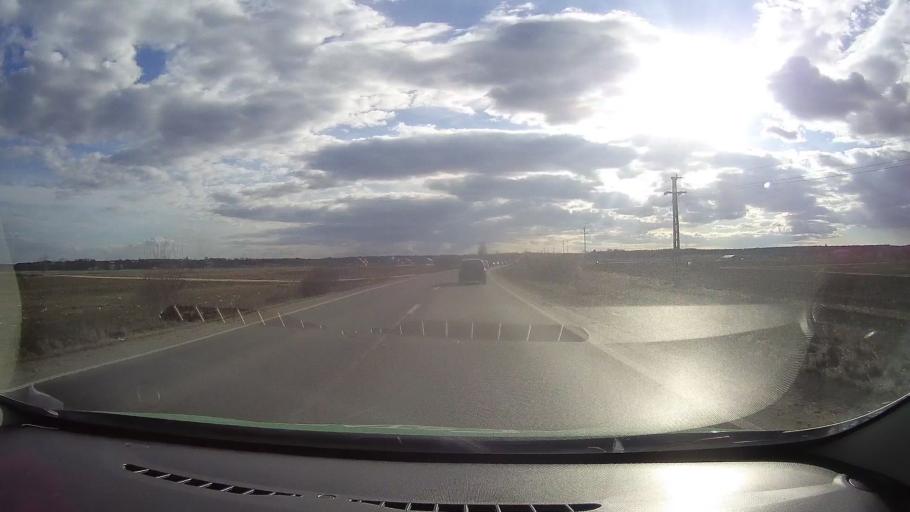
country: RO
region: Dambovita
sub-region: Comuna Lucieni
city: Lucieni
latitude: 44.8609
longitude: 25.4152
